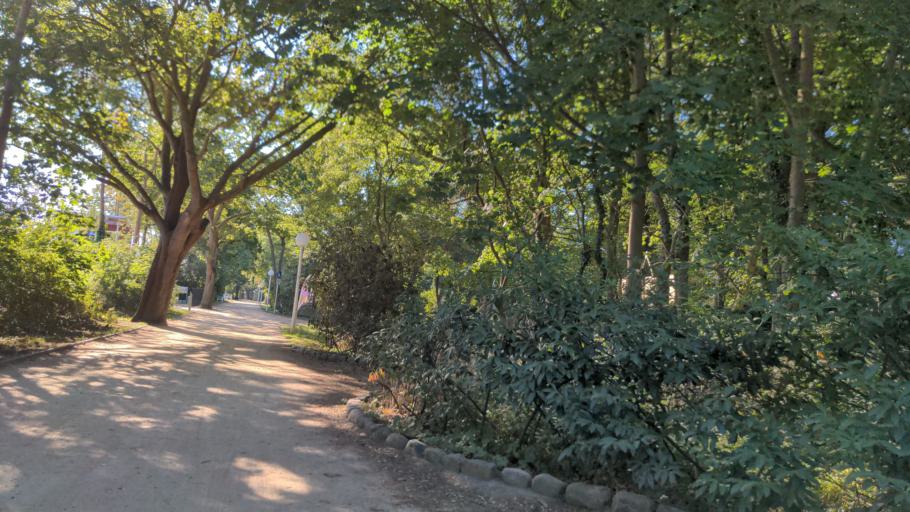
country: DE
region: Mecklenburg-Vorpommern
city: Ostseebad Boltenhagen
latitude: 53.9868
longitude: 11.2088
